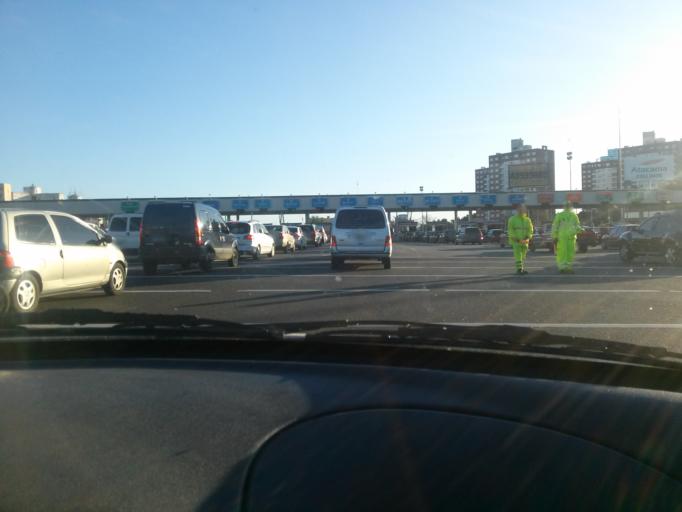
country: AR
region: Buenos Aires F.D.
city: Villa Lugano
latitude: -34.6982
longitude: -58.4957
